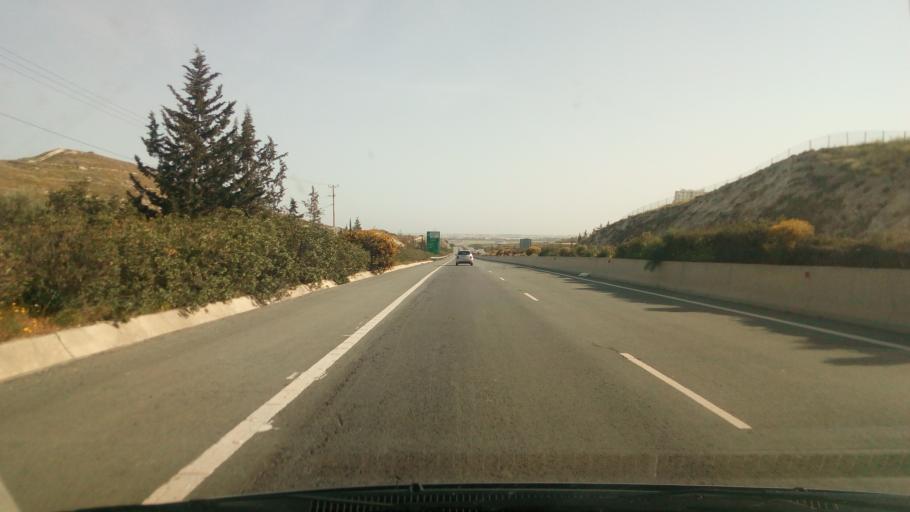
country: CY
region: Larnaka
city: Aradippou
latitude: 34.9371
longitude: 33.5637
